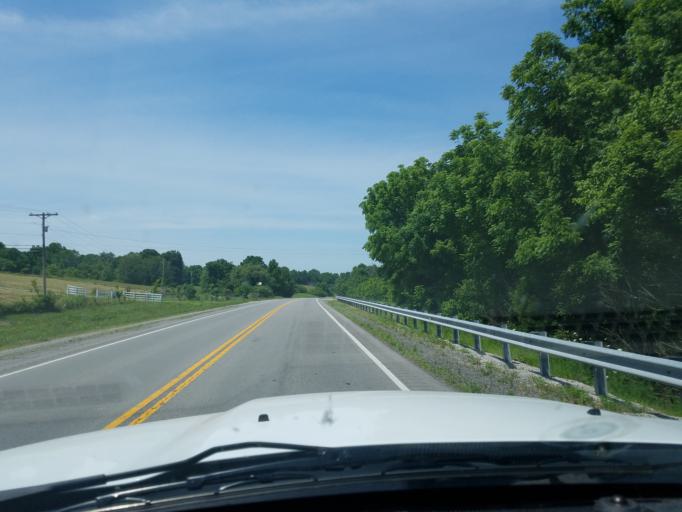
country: US
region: Kentucky
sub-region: Allen County
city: Scottsville
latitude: 36.6819
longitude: -86.2527
